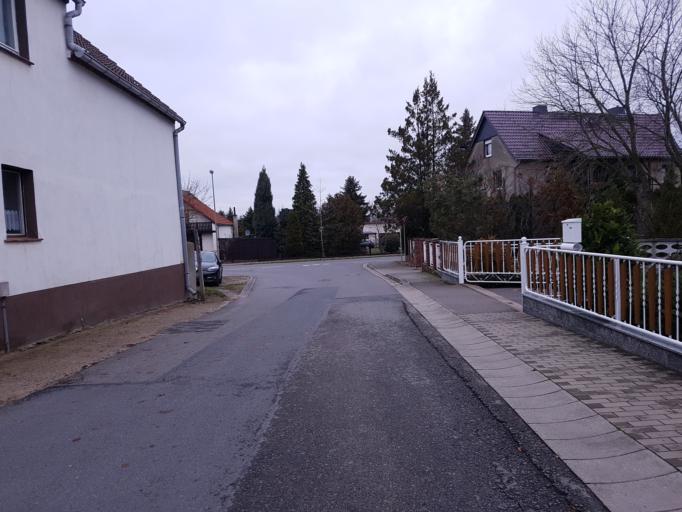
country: DE
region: Brandenburg
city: Groden
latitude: 51.4058
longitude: 13.5759
